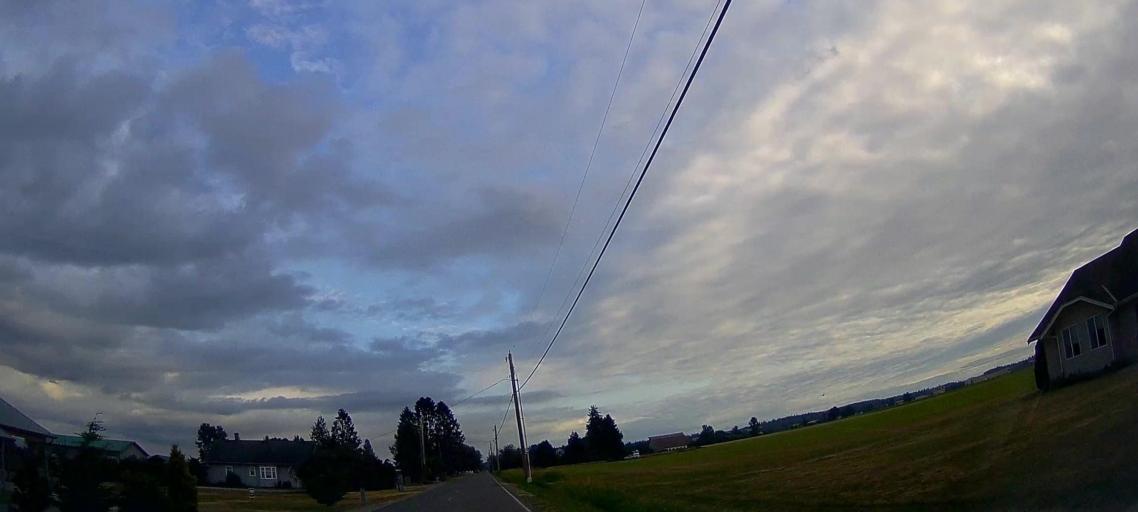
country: US
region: Washington
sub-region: Skagit County
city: Burlington
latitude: 48.5421
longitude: -122.4114
